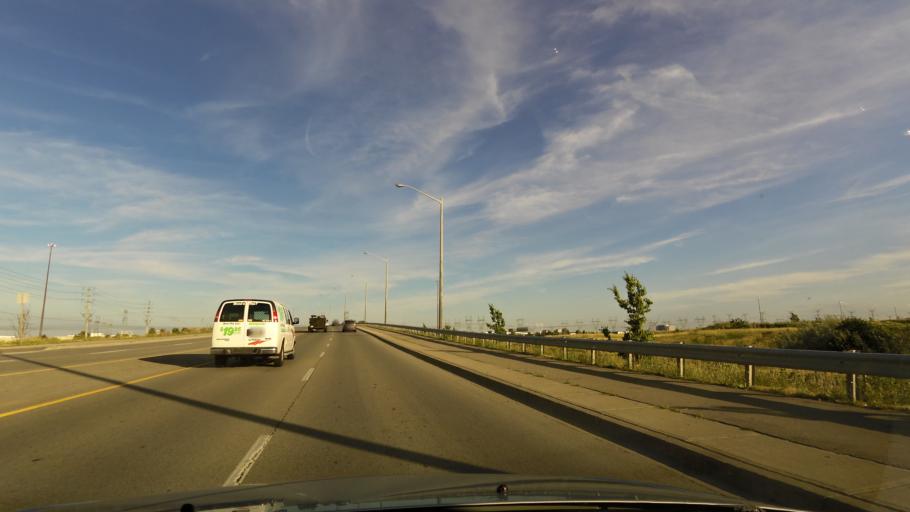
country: CA
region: Ontario
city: Brampton
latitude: 43.6648
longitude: -79.7077
